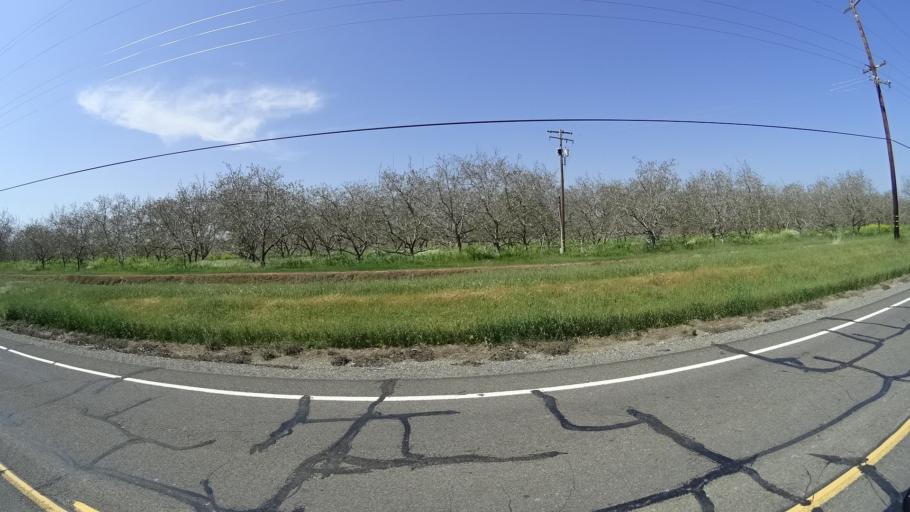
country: US
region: California
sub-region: Glenn County
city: Willows
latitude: 39.5104
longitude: -122.0171
